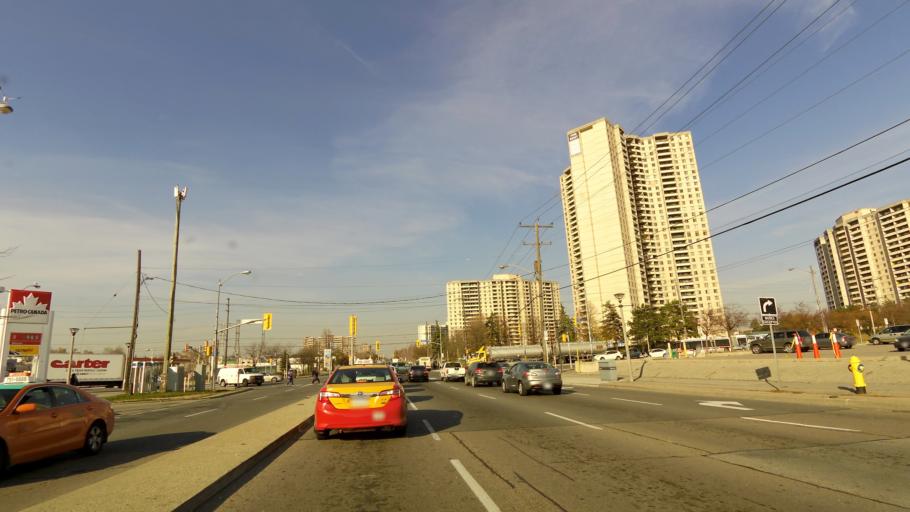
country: CA
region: Ontario
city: Concord
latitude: 43.7567
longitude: -79.5175
